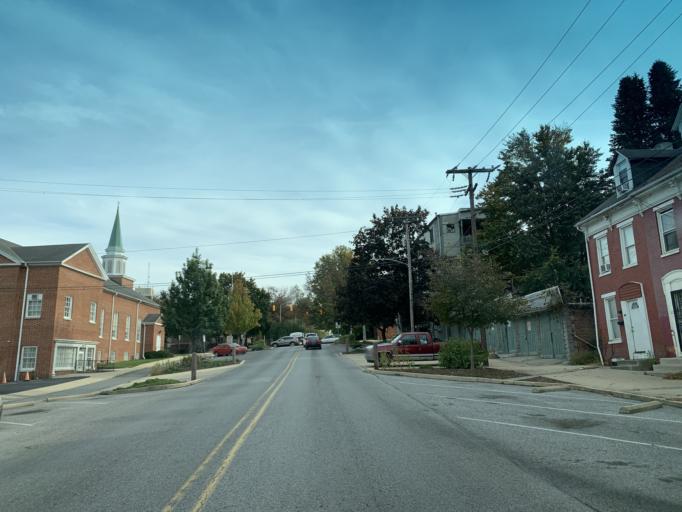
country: US
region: Pennsylvania
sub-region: York County
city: York
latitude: 39.9658
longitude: -76.7195
